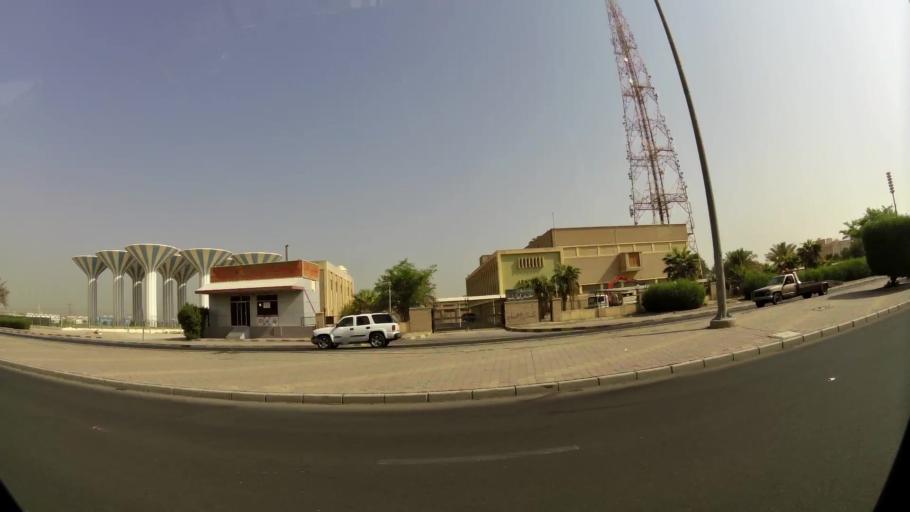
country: KW
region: Al Asimah
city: Ar Rabiyah
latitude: 29.2868
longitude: 47.8815
